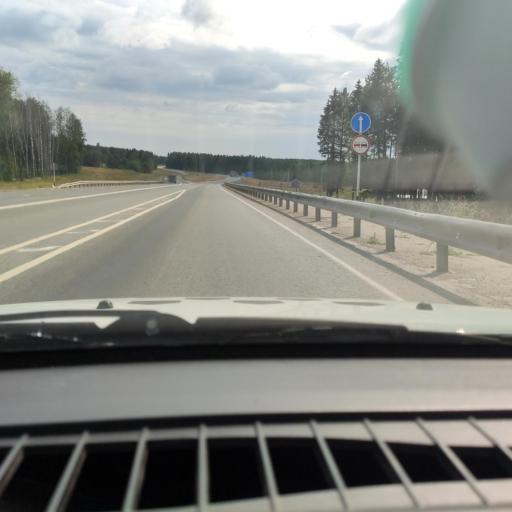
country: RU
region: Perm
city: Berezniki
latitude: 59.4019
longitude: 56.8799
